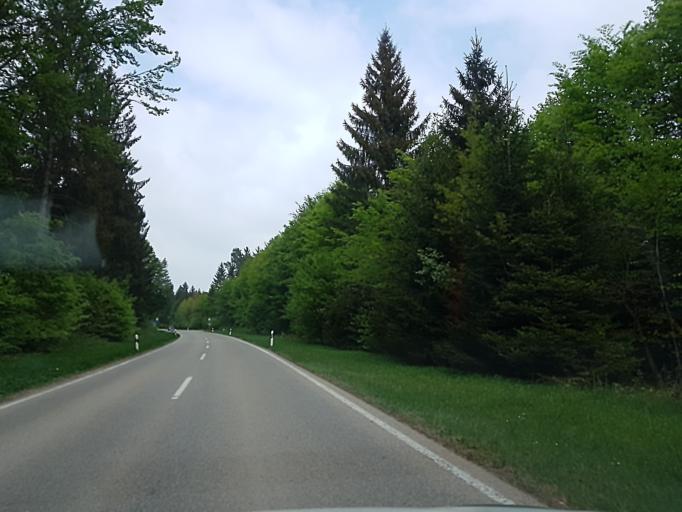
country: DE
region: Bavaria
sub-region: Upper Bavaria
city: Hohenlinden
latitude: 48.1348
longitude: 11.9833
